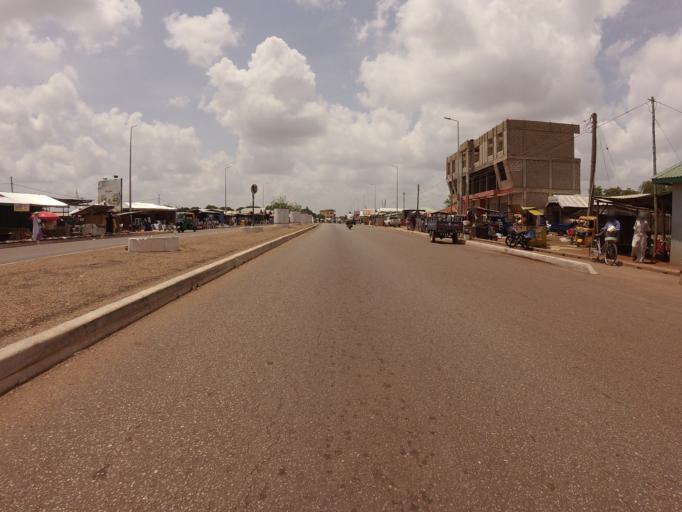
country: GH
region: Northern
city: Tamale
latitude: 9.3969
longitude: -0.8457
